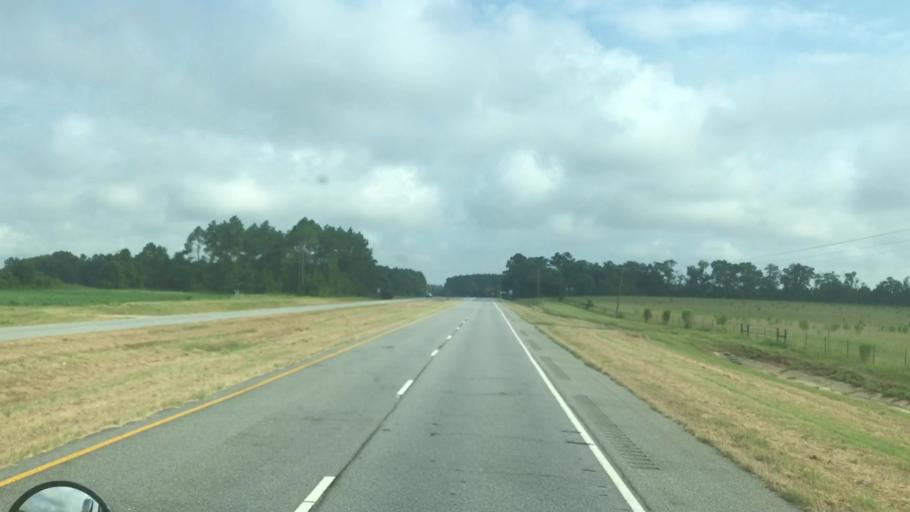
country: US
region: Georgia
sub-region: Miller County
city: Colquitt
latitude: 31.2203
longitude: -84.7789
